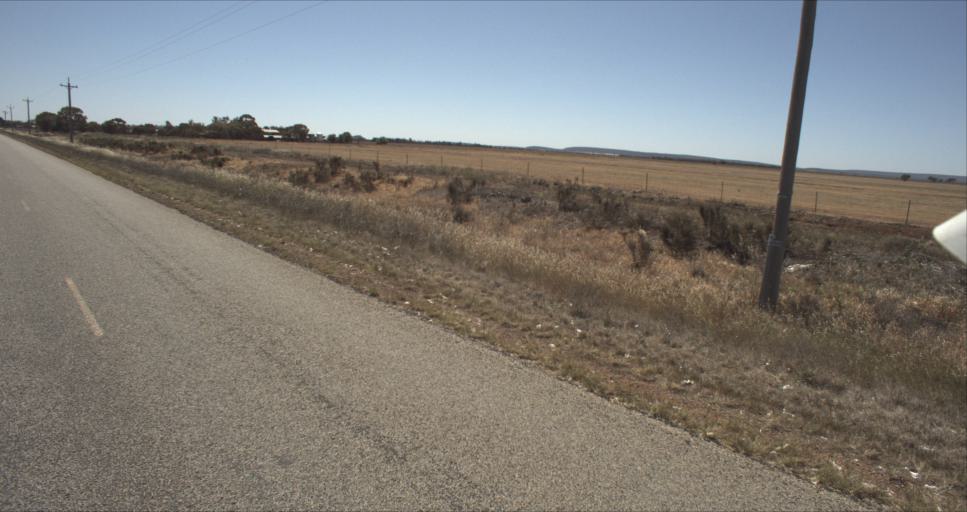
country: AU
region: New South Wales
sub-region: Leeton
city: Leeton
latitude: -34.4507
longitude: 146.2960
